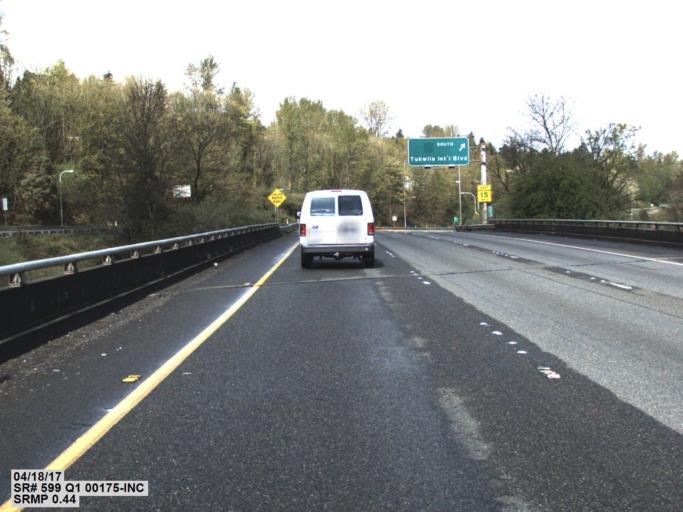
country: US
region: Washington
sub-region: King County
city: Riverton
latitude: 47.4868
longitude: -122.2770
